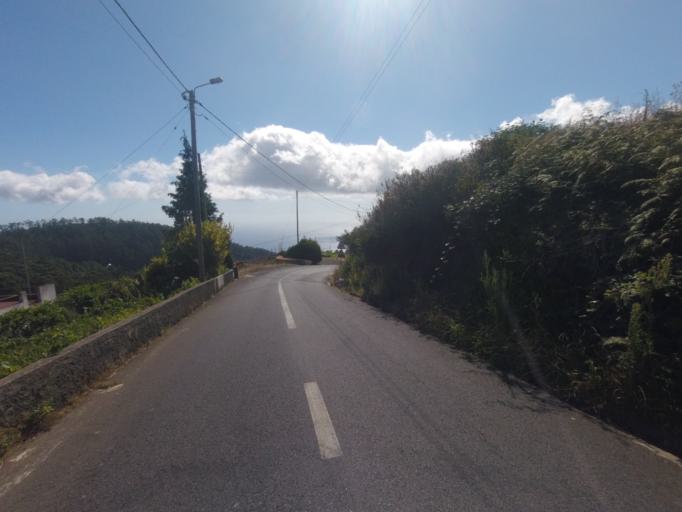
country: PT
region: Madeira
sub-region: Ribeira Brava
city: Campanario
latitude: 32.6947
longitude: -17.0275
